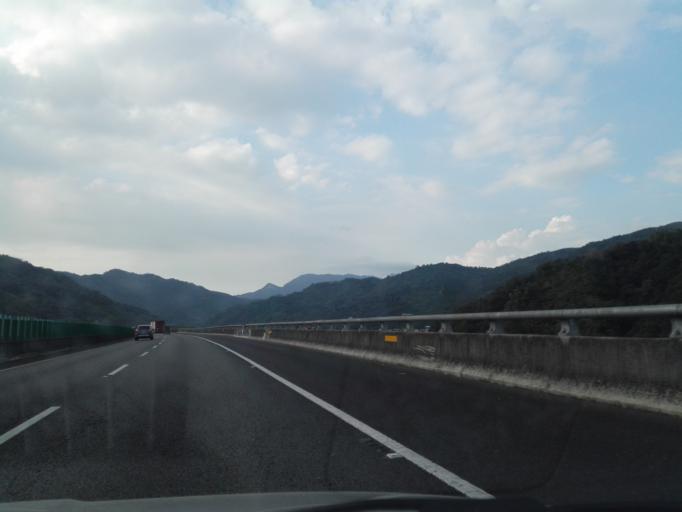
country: TW
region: Taiwan
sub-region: Nantou
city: Puli
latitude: 23.9816
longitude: 120.8646
